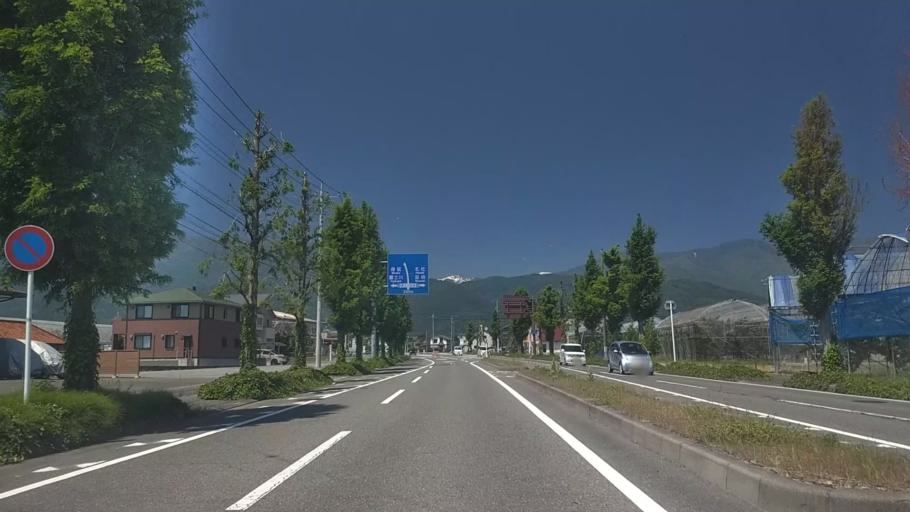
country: JP
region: Yamanashi
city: Ryuo
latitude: 35.6383
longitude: 138.4682
